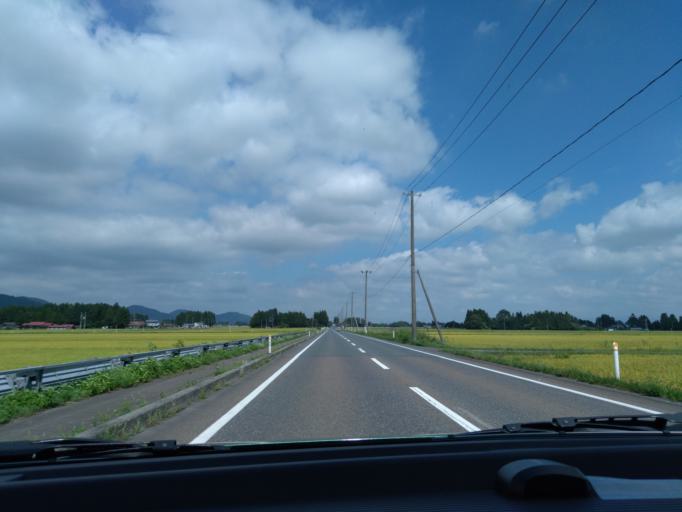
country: JP
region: Iwate
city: Hanamaki
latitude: 39.3932
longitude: 141.0591
